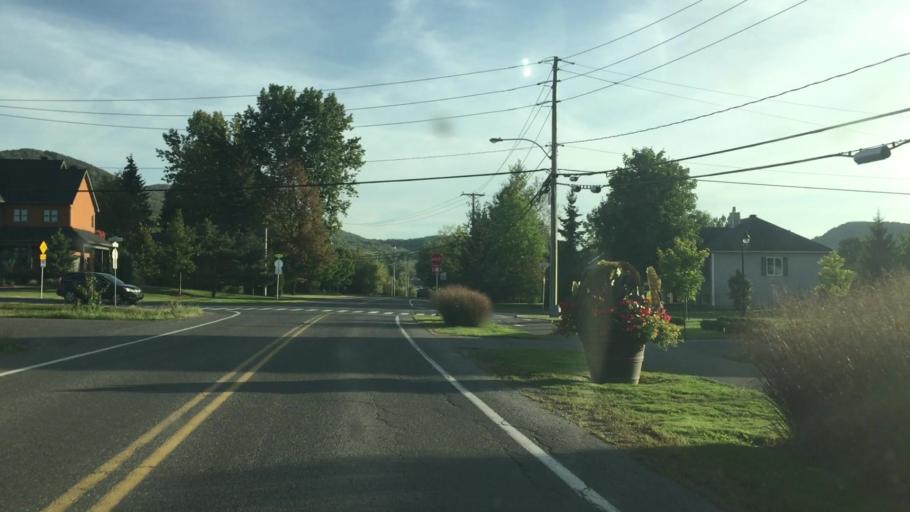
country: CA
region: Quebec
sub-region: Monteregie
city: Bromont
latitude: 45.3094
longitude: -72.6576
